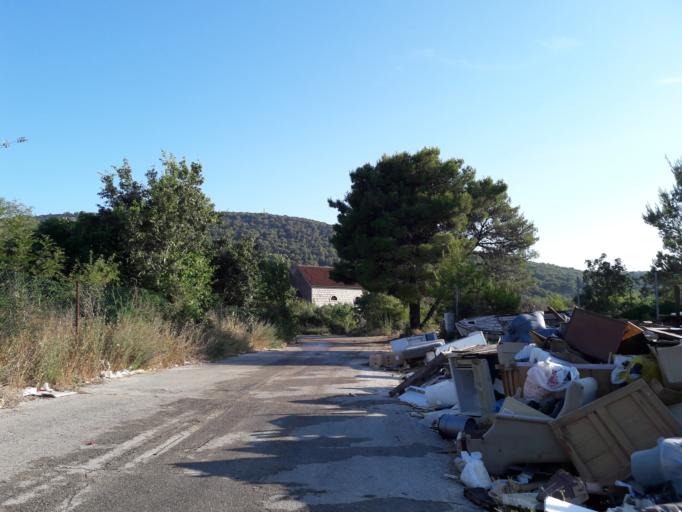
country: HR
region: Sibensko-Kniniska
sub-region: Grad Sibenik
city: Sibenik
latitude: 43.6951
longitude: 15.8455
